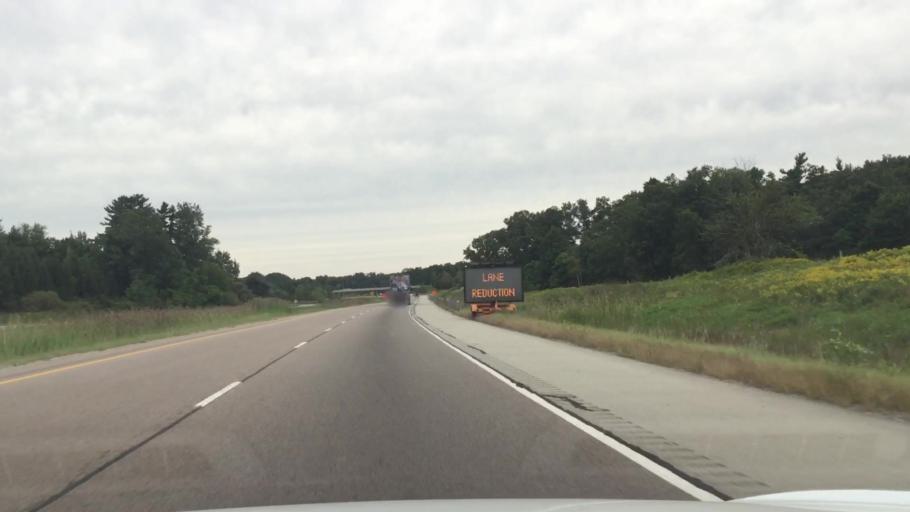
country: CA
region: Ontario
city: Delaware
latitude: 42.9167
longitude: -81.4580
